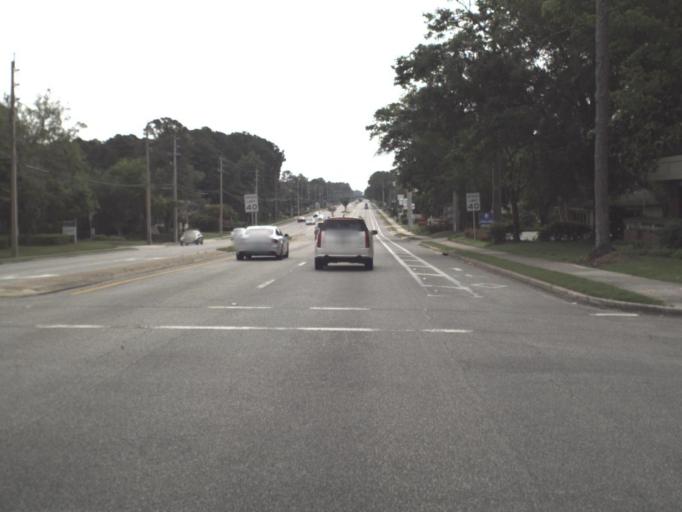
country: US
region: Florida
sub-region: Clay County
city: Bellair-Meadowbrook Terrace
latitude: 30.1649
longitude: -81.7302
